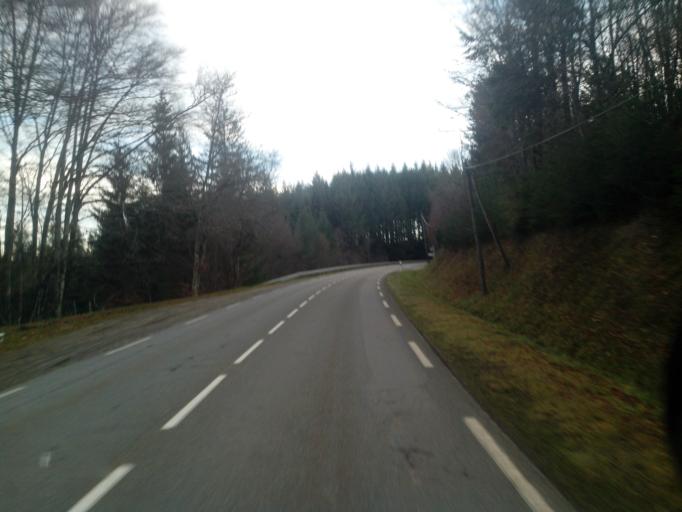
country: FR
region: Limousin
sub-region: Departement de la Correze
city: Meymac
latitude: 45.5772
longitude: 2.1357
